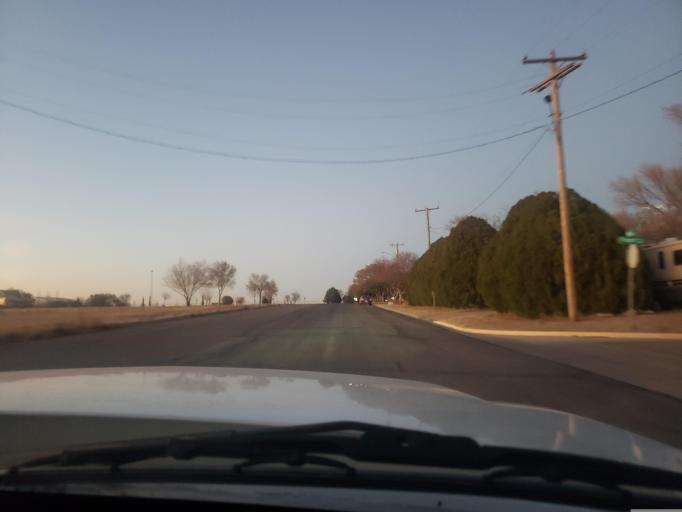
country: US
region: Kansas
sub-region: Finney County
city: Garden City
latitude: 37.9911
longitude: -100.8694
